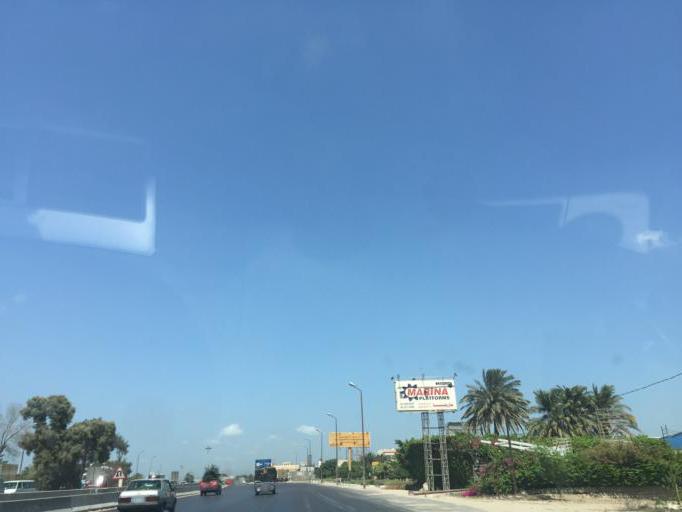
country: EG
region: Alexandria
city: Alexandria
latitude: 31.0760
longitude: 29.8379
